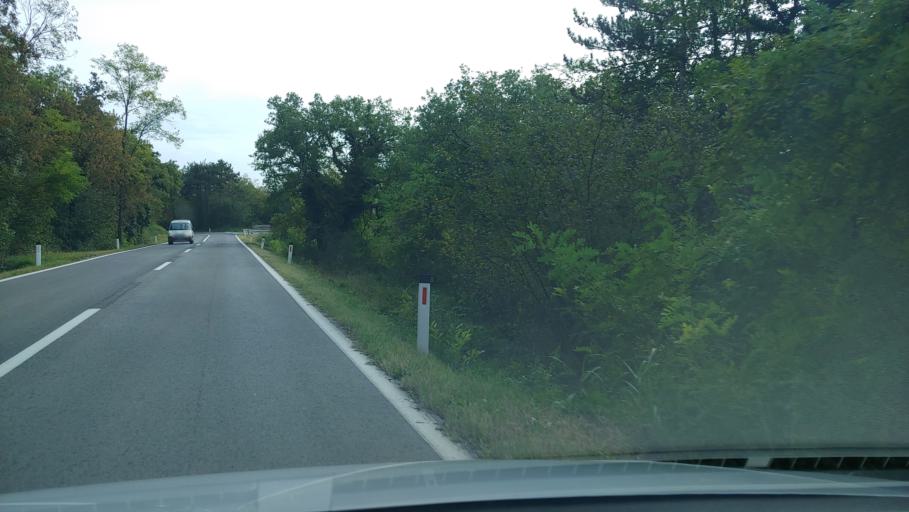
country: SI
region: Nova Gorica
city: Sempas
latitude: 45.9018
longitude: 13.7805
